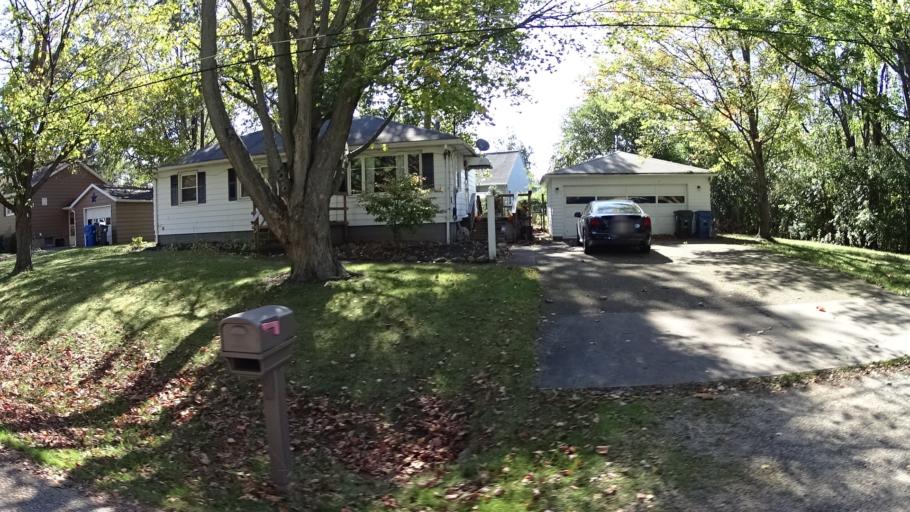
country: US
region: Ohio
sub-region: Lorain County
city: Amherst
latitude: 41.3895
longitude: -82.2196
